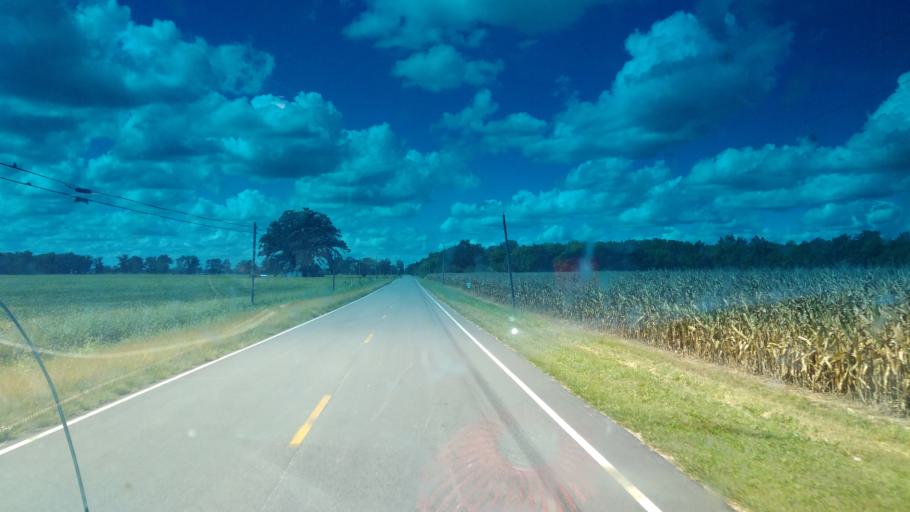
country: US
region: Ohio
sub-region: Champaign County
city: North Lewisburg
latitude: 40.1888
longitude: -83.4630
